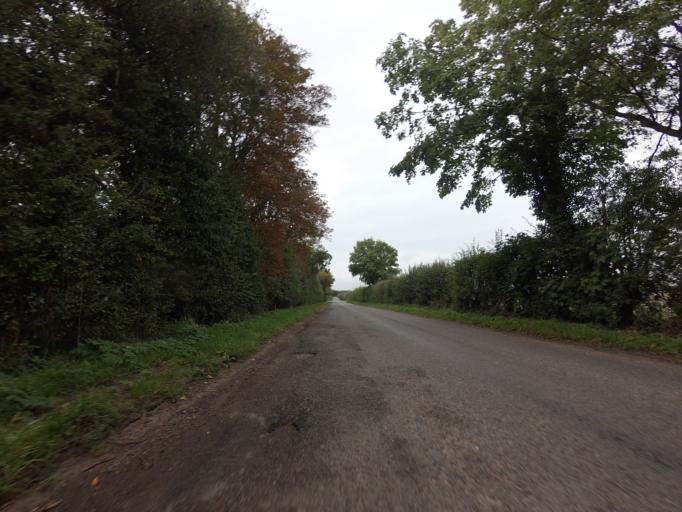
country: GB
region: England
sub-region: Cambridgeshire
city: Duxford
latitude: 52.0668
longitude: 0.1040
